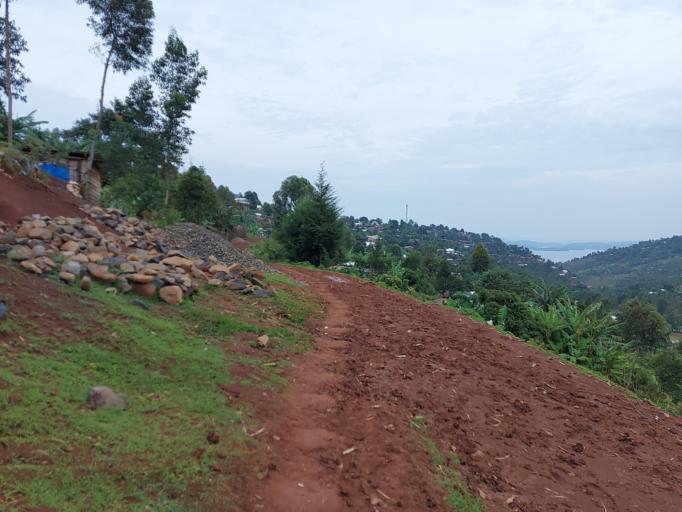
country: CD
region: South Kivu
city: Bukavu
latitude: -2.4868
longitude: 28.8180
